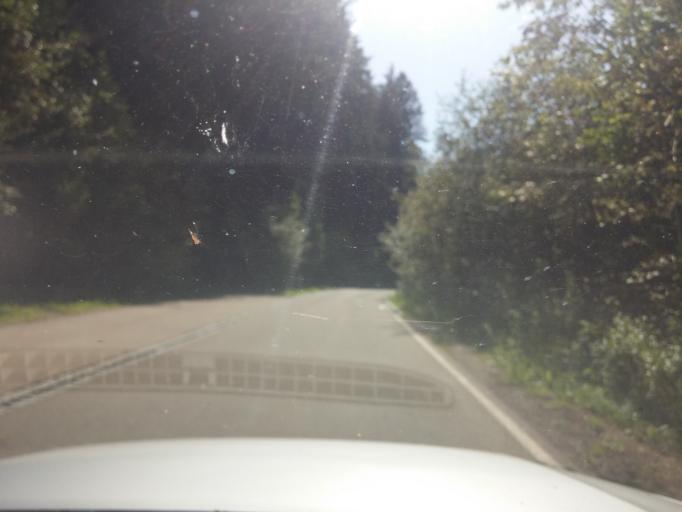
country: DE
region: Bavaria
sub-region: Swabia
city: Lautrach
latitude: 47.8733
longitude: 10.1028
